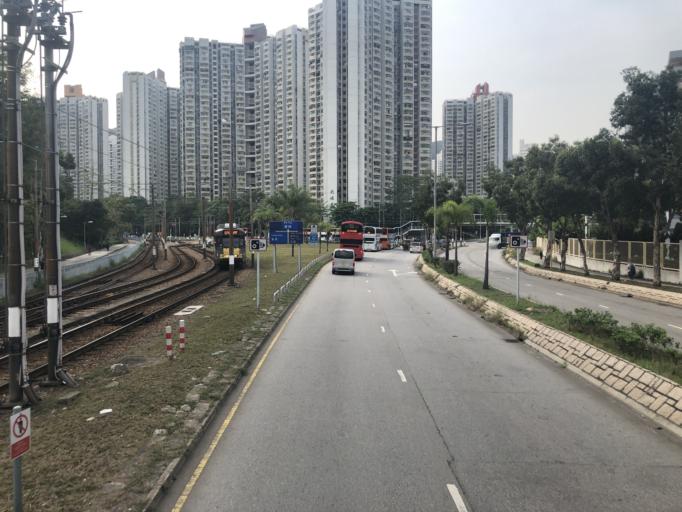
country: HK
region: Tuen Mun
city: Tuen Mun
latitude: 22.4035
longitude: 113.9668
